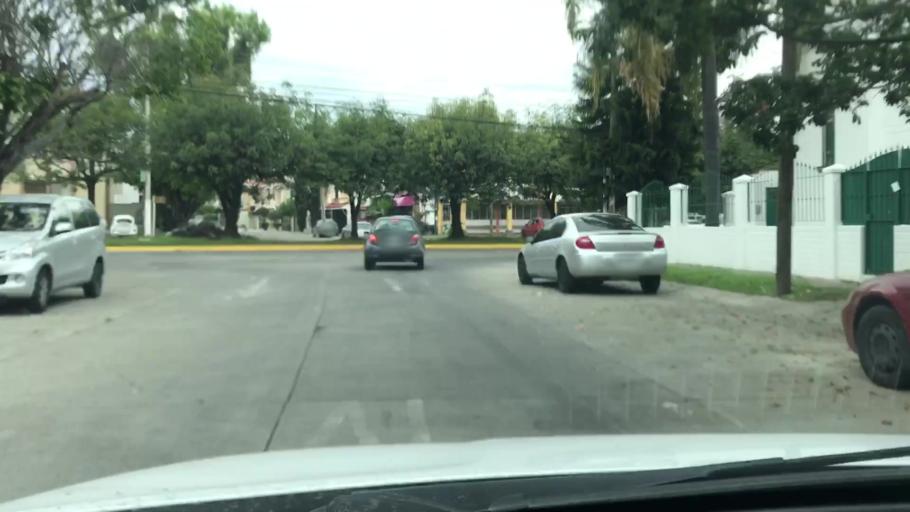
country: MX
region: Jalisco
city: Guadalajara
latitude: 20.6361
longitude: -103.4319
